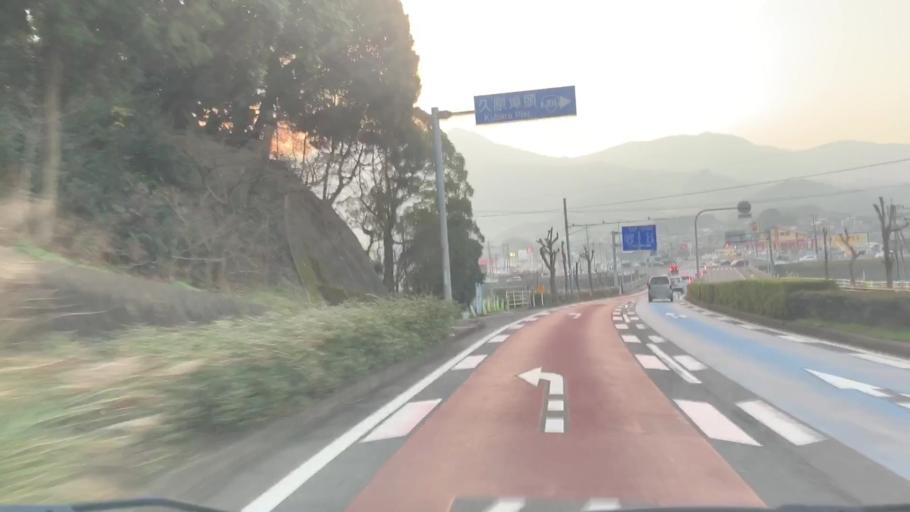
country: JP
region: Saga Prefecture
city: Imaricho-ko
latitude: 33.2632
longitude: 129.8617
